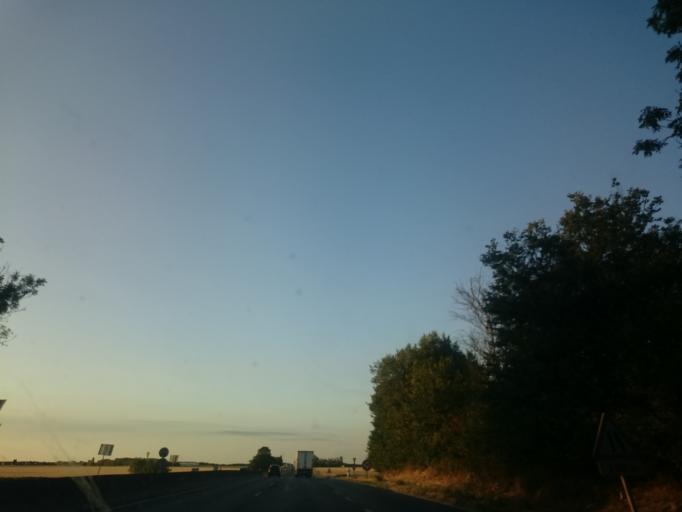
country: FR
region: Ile-de-France
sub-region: Departement de l'Essonne
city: Chamarande
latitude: 48.5155
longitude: 2.2037
